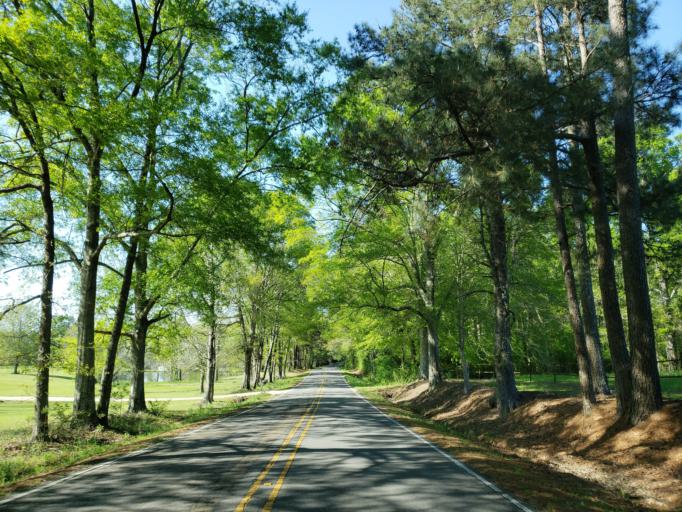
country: US
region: Mississippi
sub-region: Forrest County
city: Rawls Springs
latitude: 31.5048
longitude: -89.3600
